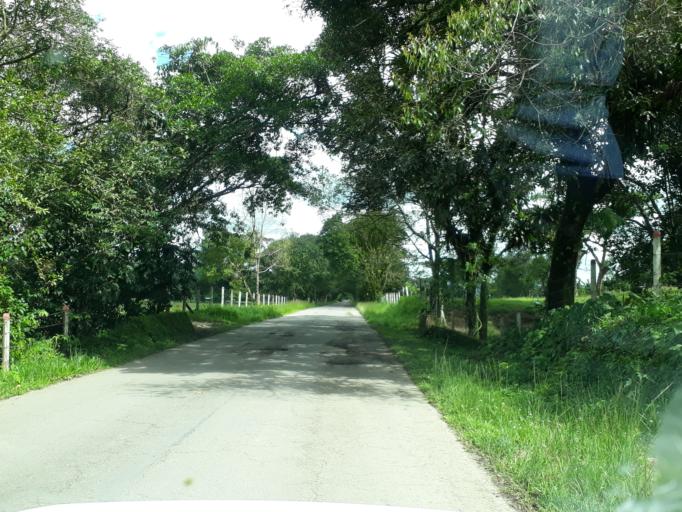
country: CO
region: Cundinamarca
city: Medina
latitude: 4.5395
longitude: -73.3574
